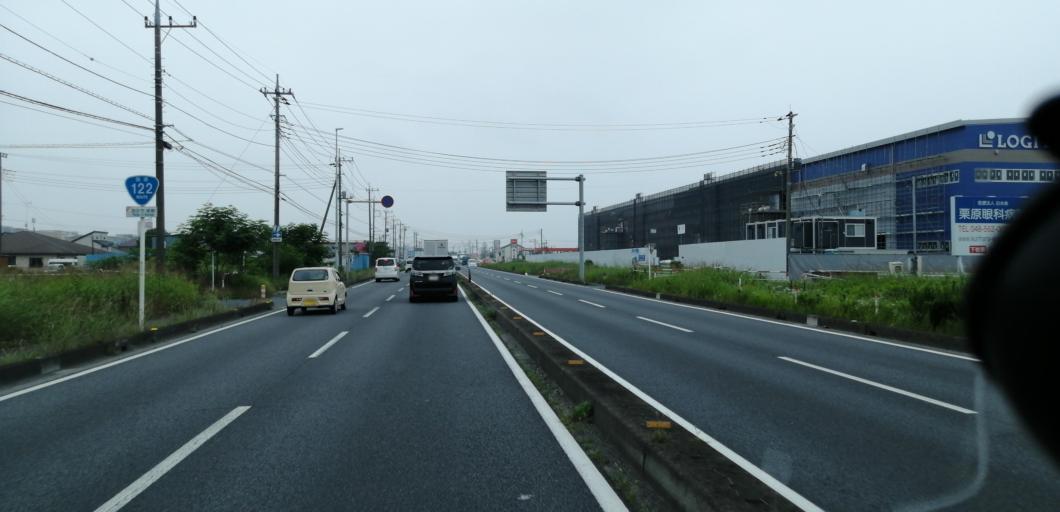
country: JP
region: Saitama
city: Hanyu
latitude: 36.1436
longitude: 139.5514
